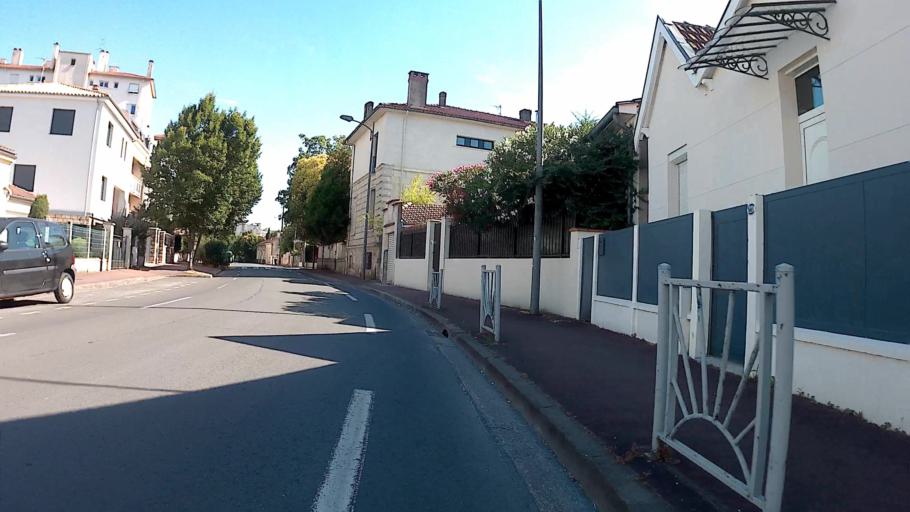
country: FR
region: Aquitaine
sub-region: Departement de la Gironde
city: Le Bouscat
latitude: 44.8636
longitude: -0.5976
